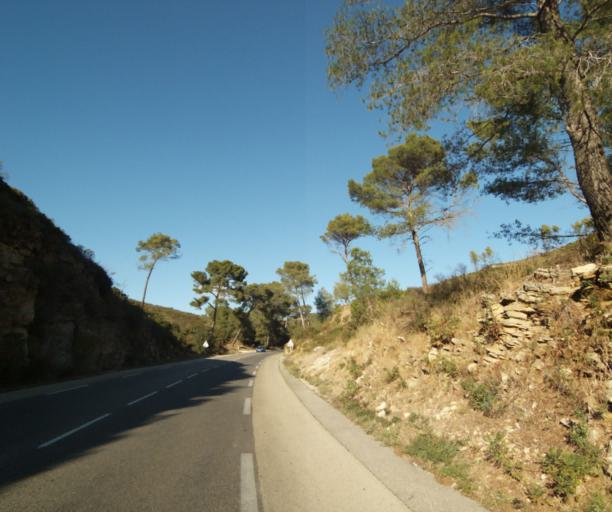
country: FR
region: Provence-Alpes-Cote d'Azur
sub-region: Departement des Bouches-du-Rhone
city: Cassis
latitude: 43.2107
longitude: 5.5798
